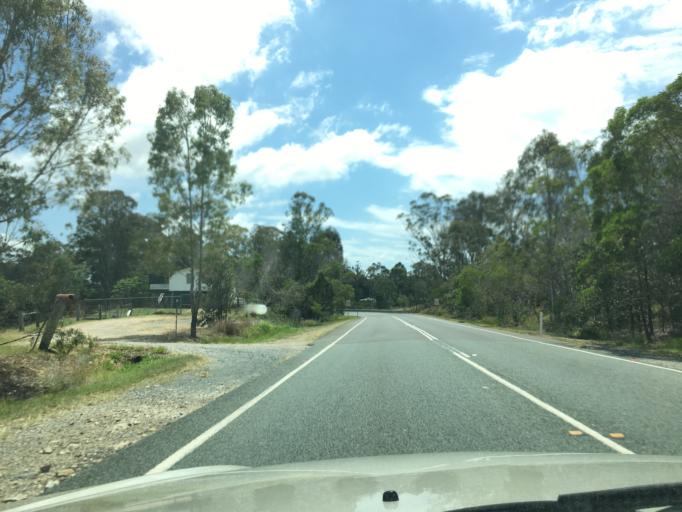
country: AU
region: Queensland
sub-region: Logan
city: Waterford West
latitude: -27.7028
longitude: 153.1477
